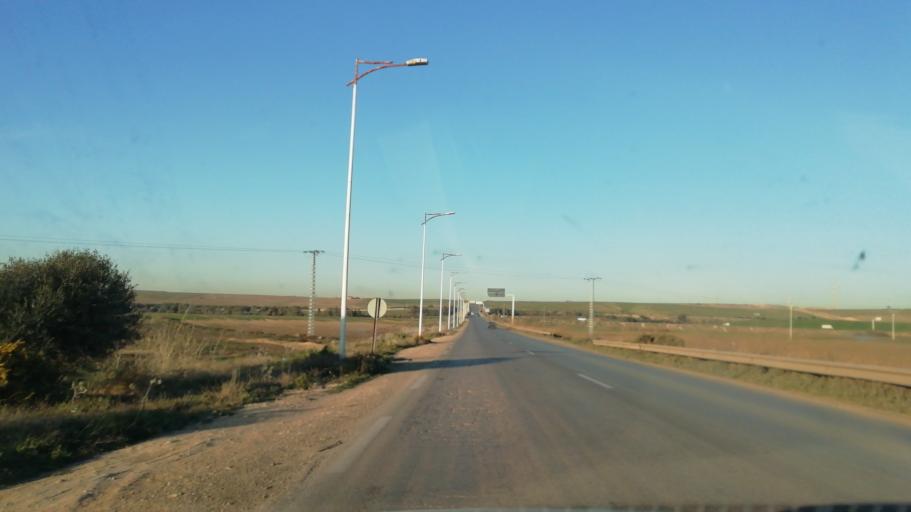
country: DZ
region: Oran
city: Sidi ech Chahmi
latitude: 35.5668
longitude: -0.5600
